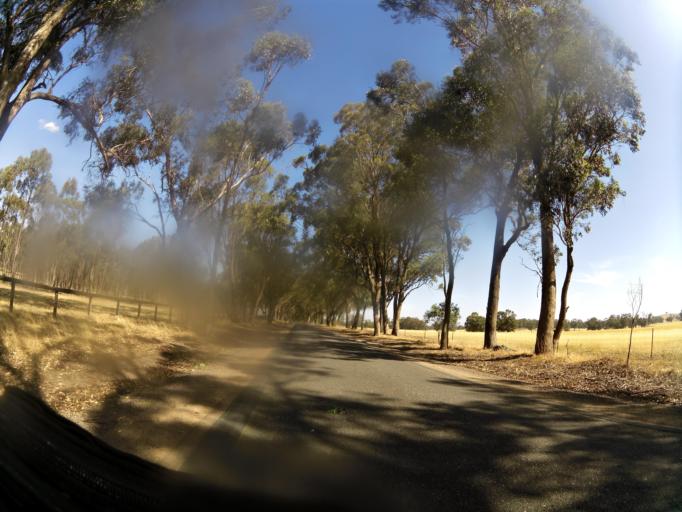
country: AU
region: Victoria
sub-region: Campaspe
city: Kyabram
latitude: -36.8872
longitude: 145.1008
